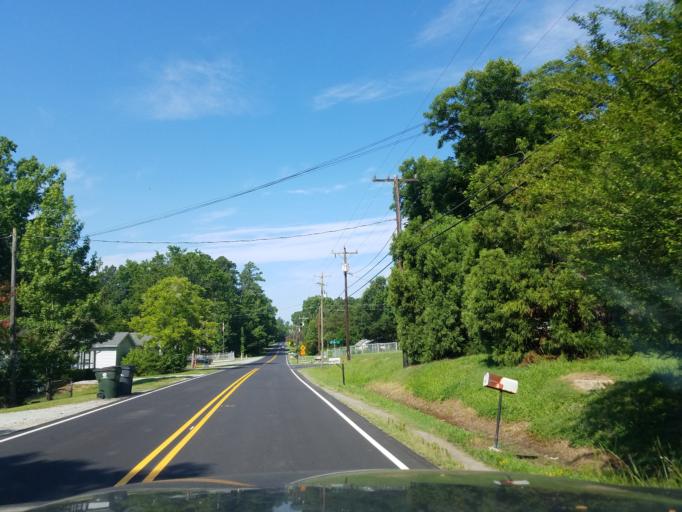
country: US
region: North Carolina
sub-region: Durham County
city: Gorman
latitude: 36.0302
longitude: -78.8314
